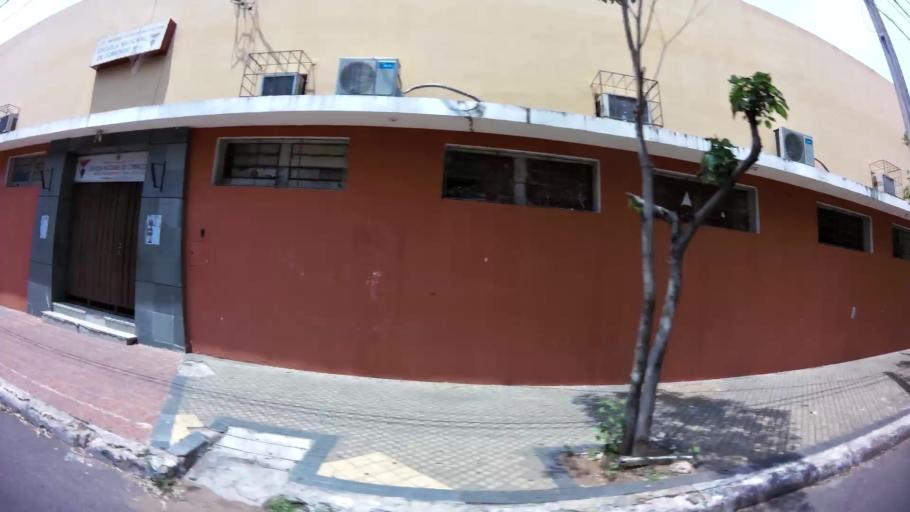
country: PY
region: Asuncion
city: Asuncion
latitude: -25.2943
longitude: -57.6175
